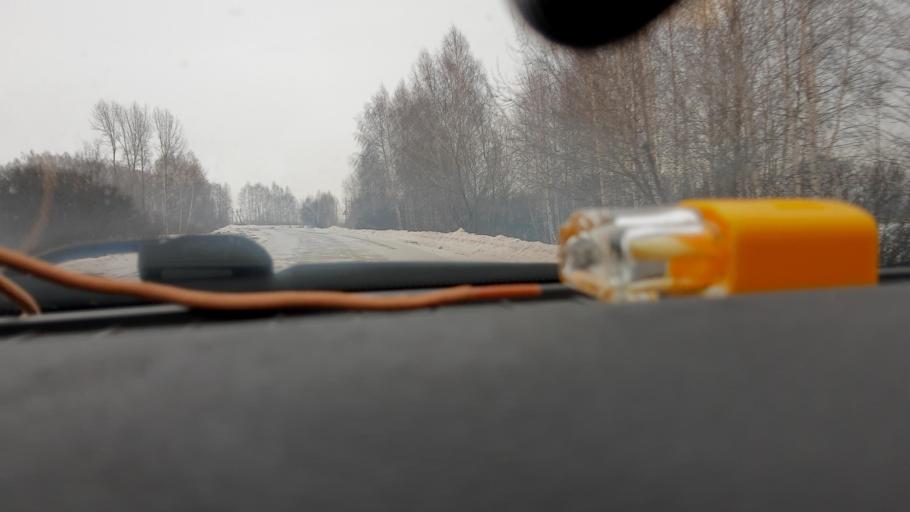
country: RU
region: Bashkortostan
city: Ulukulevo
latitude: 54.5003
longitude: 56.4020
